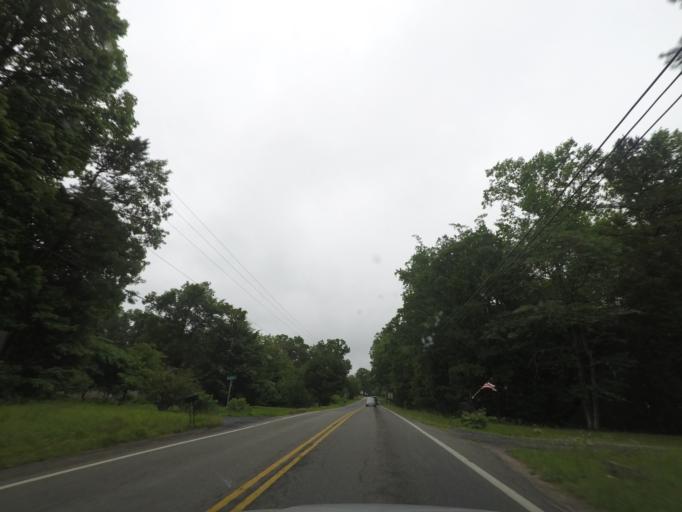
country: US
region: Virginia
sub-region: Fluvanna County
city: Weber City
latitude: 37.7803
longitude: -78.2391
